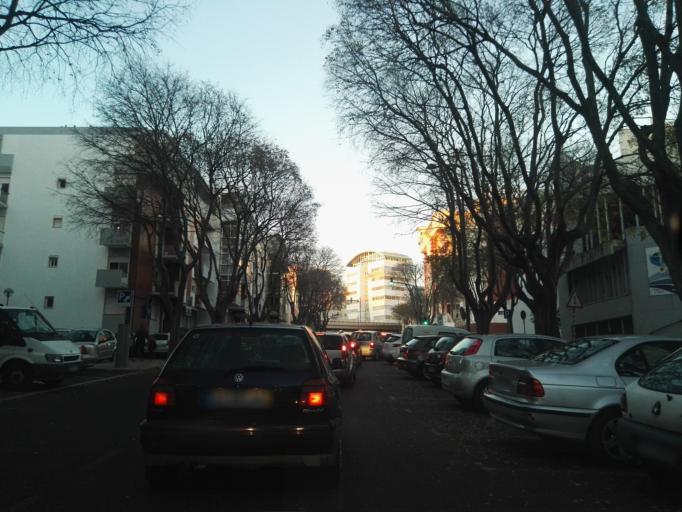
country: PT
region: Lisbon
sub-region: Oeiras
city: Paco de Arcos
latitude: 38.6957
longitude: -9.2928
